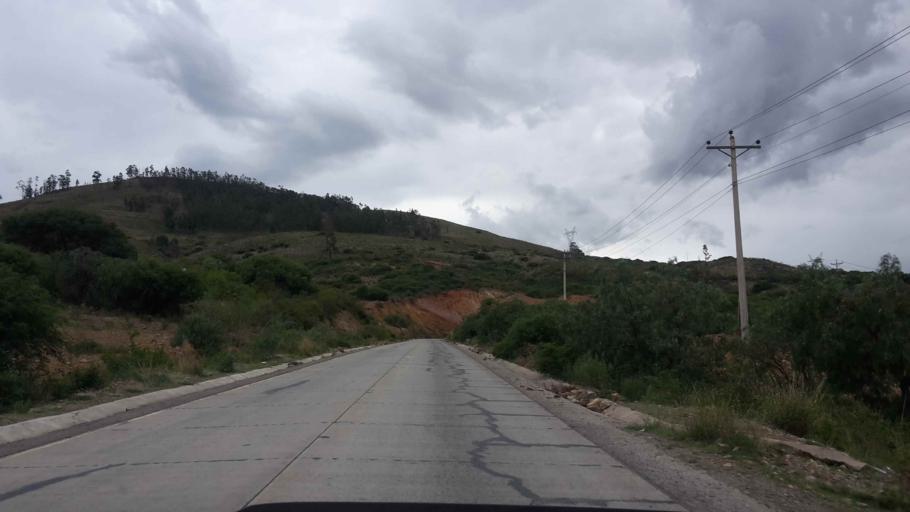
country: BO
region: Cochabamba
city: Cochabamba
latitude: -17.5329
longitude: -66.2020
